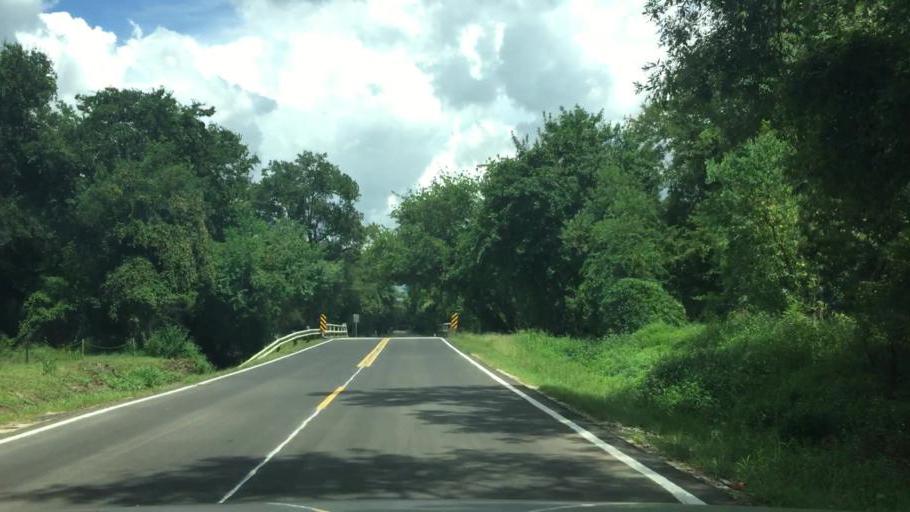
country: US
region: Texas
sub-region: Harris County
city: Jersey Village
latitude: 29.8133
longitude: -95.6341
